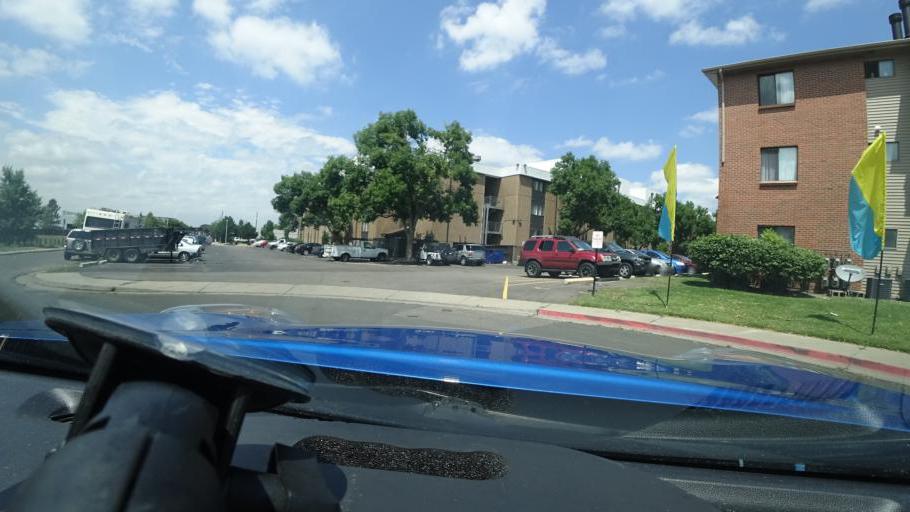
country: US
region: Colorado
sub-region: Adams County
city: Aurora
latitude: 39.7075
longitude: -104.8626
